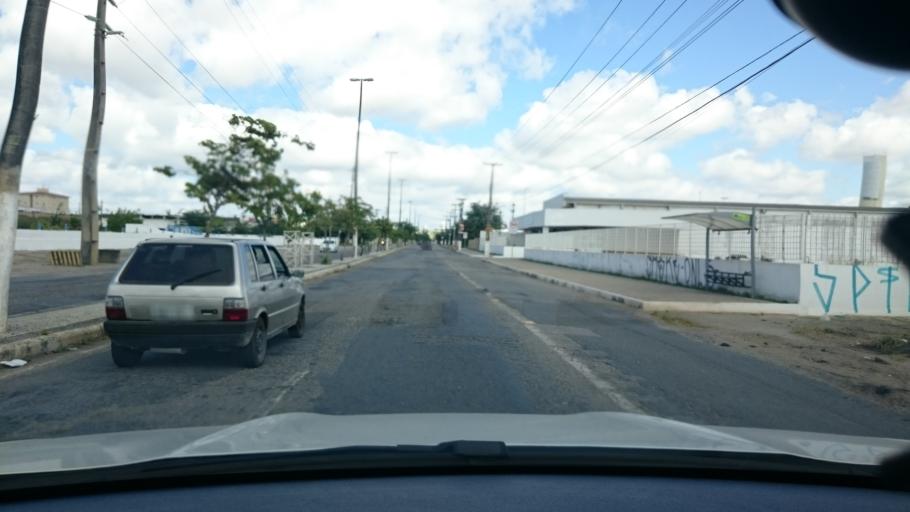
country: BR
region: Paraiba
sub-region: Campina Grande
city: Campina Grande
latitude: -7.2342
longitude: -35.9164
